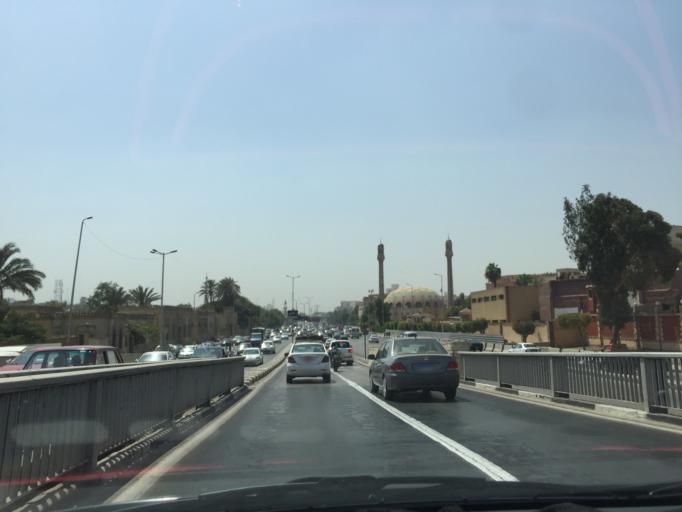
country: EG
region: Muhafazat al Qahirah
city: Cairo
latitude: 30.0540
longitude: 31.2785
